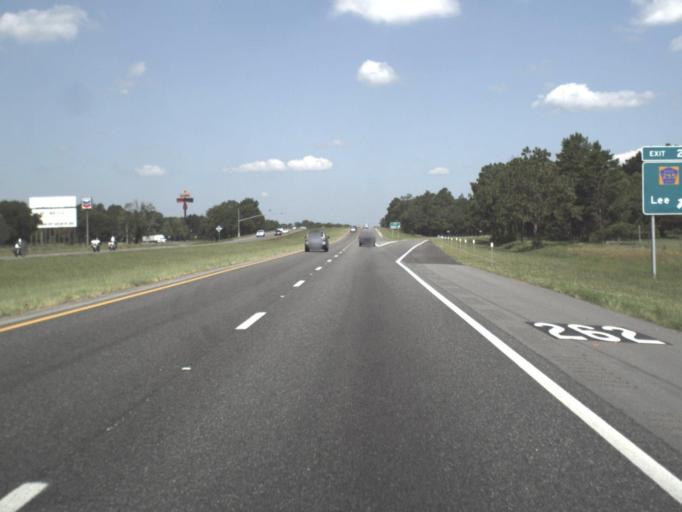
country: US
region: Florida
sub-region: Madison County
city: Madison
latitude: 30.3786
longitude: -83.2919
